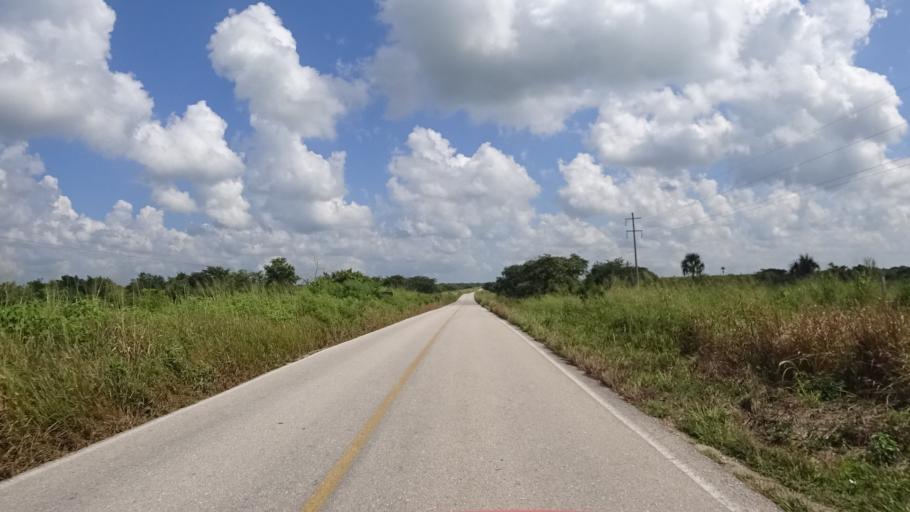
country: MX
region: Yucatan
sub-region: Panaba
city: Loche
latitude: 21.3442
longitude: -88.1554
